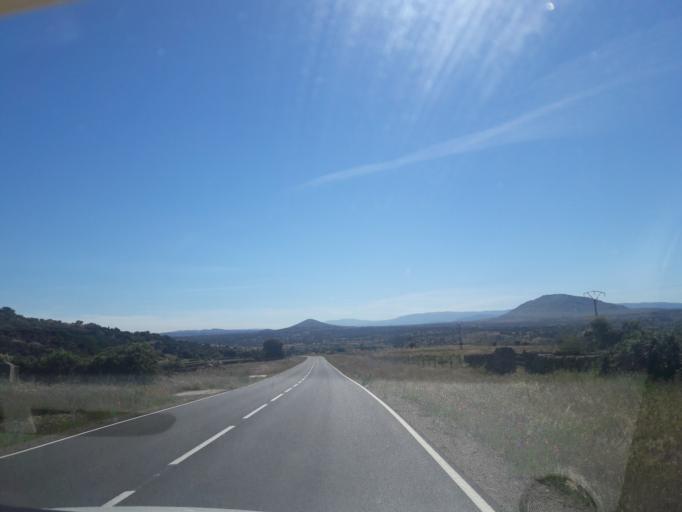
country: ES
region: Castille and Leon
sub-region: Provincia de Salamanca
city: Santibanez de Bejar
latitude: 40.4808
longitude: -5.6369
